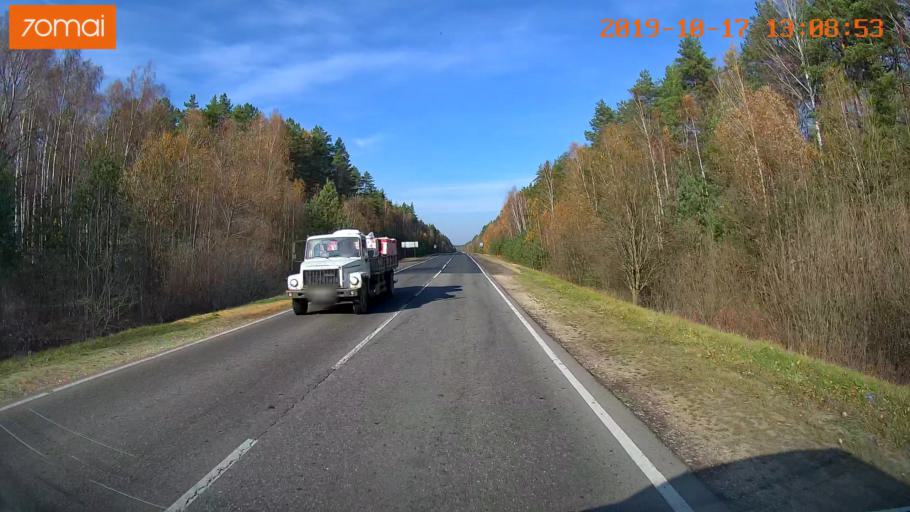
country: RU
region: Rjazan
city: Syntul
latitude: 54.9955
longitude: 41.2665
